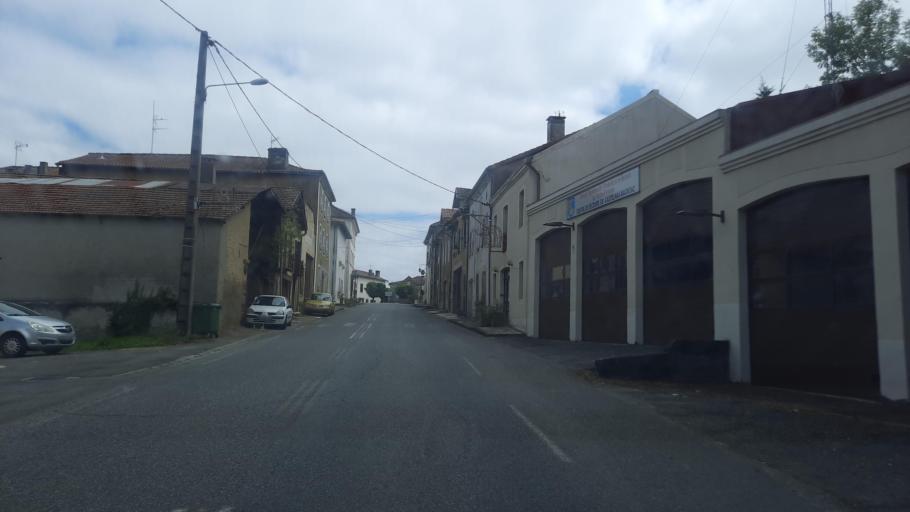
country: FR
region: Midi-Pyrenees
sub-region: Departement des Hautes-Pyrenees
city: Trie-sur-Baise
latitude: 43.2948
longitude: 0.5038
